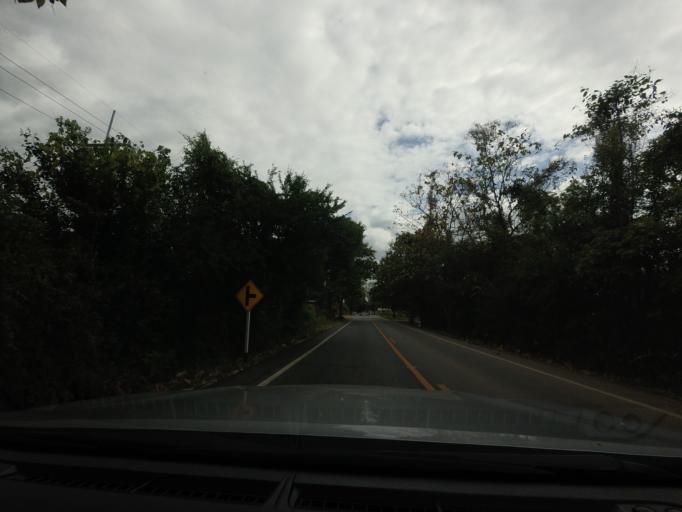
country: TH
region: Phitsanulok
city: Noen Maprang
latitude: 16.6894
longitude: 100.5300
